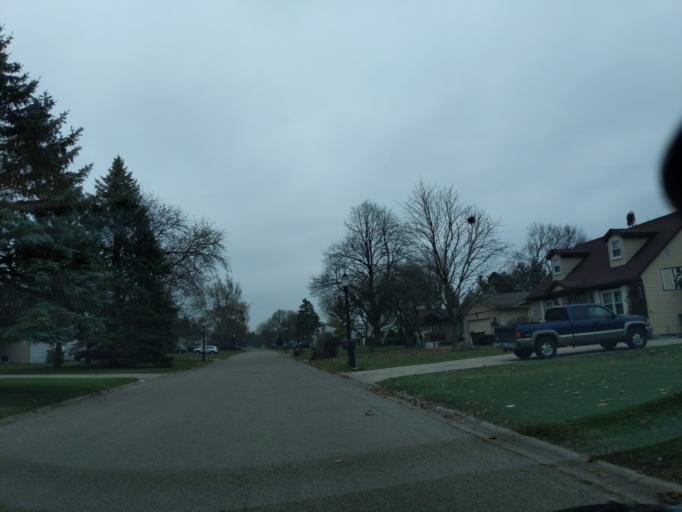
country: US
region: Michigan
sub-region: Eaton County
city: Waverly
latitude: 42.7317
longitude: -84.6318
